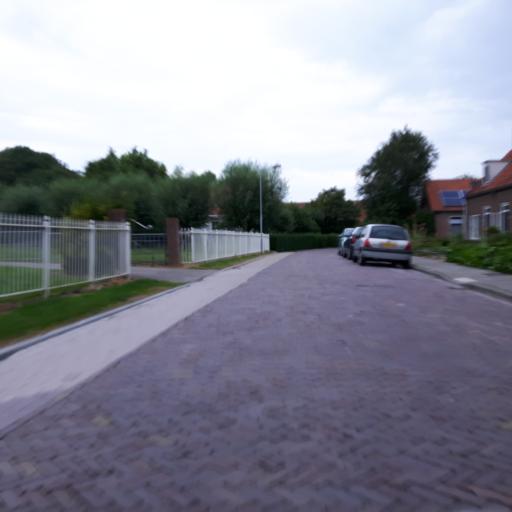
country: NL
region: Zeeland
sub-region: Gemeente Goes
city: Goes
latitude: 51.4977
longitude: 3.9233
